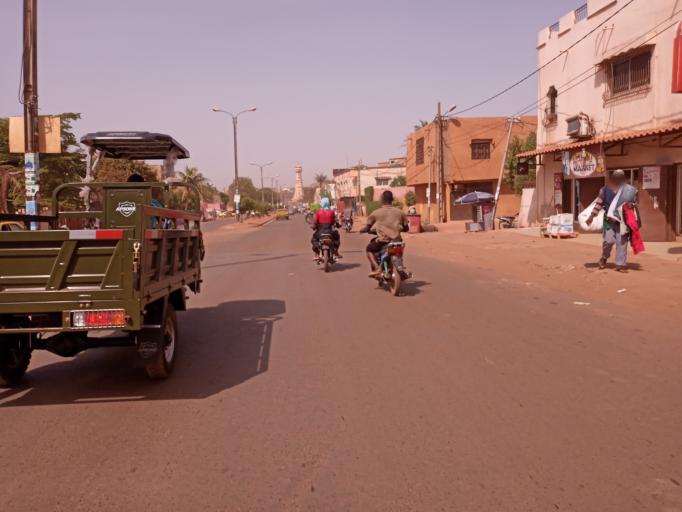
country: ML
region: Bamako
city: Bamako
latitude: 12.5802
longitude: -7.9468
